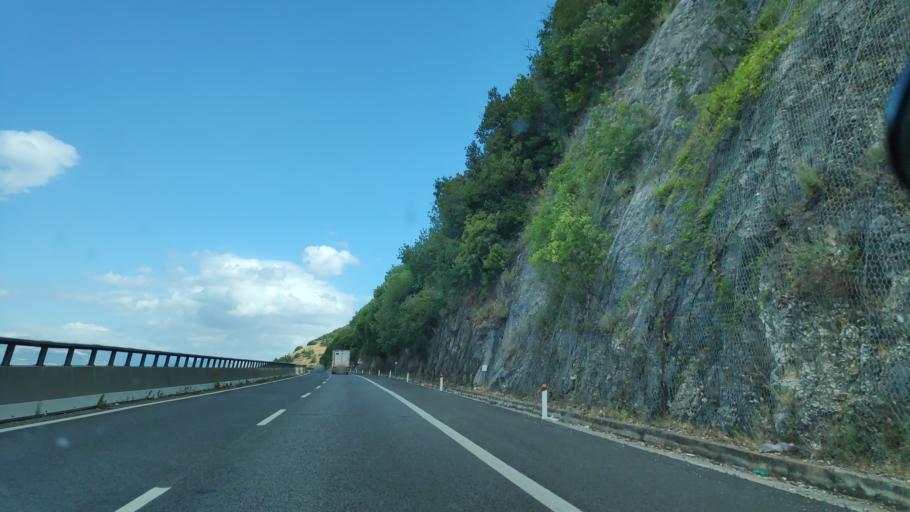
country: IT
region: Campania
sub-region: Provincia di Salerno
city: Sicignano degli Alburni
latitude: 40.5885
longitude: 15.3341
